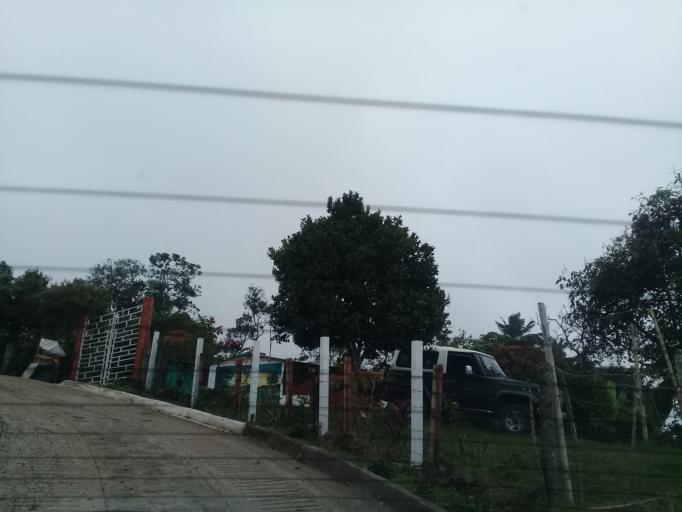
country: CO
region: Cundinamarca
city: Viani
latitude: 4.8396
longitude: -74.5534
